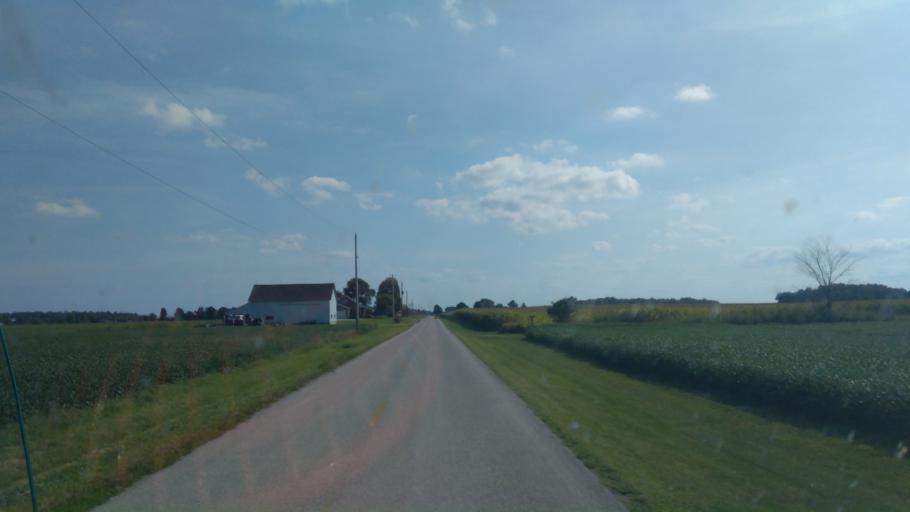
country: US
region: Ohio
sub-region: Hardin County
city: Forest
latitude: 40.7115
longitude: -83.5144
